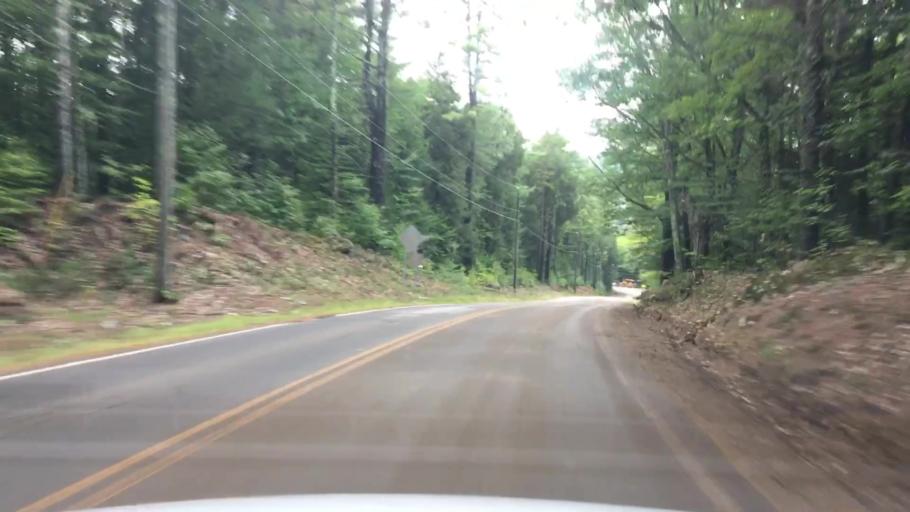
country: US
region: New Hampshire
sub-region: Carroll County
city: Effingham
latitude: 43.7735
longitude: -70.9995
